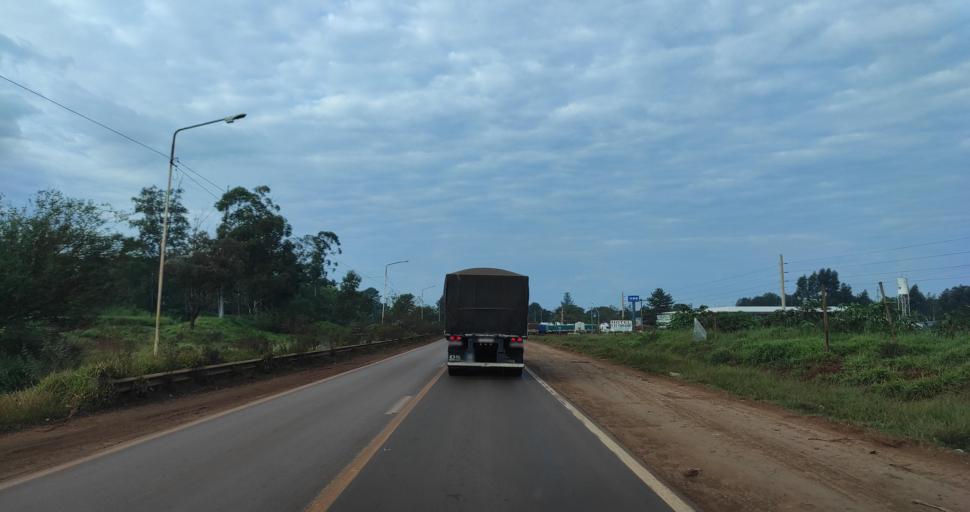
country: AR
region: Corrientes
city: Gobernador Ingeniero Valentin Virasoro
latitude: -28.0235
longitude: -56.0151
